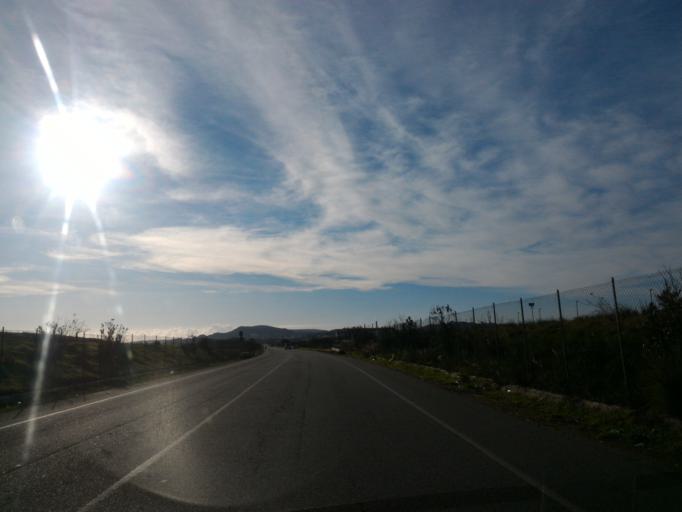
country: IT
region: Calabria
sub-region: Provincia di Crotone
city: Crotone
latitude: 39.0992
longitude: 17.1088
